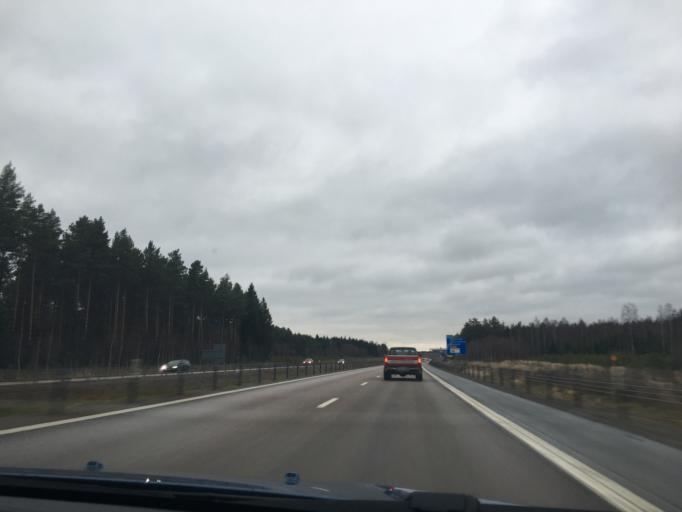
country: SE
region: Uppsala
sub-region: Alvkarleby Kommun
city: AElvkarleby
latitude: 60.4519
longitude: 17.4156
